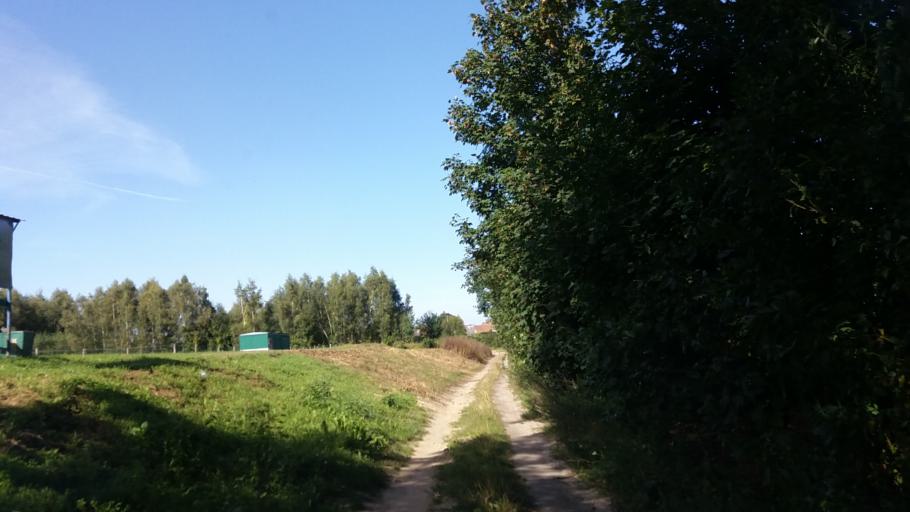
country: PL
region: West Pomeranian Voivodeship
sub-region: Powiat choszczenski
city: Krzecin
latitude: 53.1353
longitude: 15.5039
